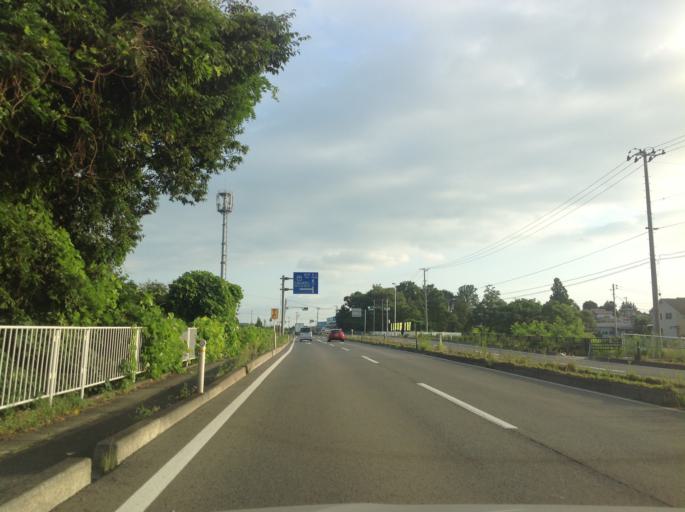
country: JP
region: Iwate
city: Hanamaki
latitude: 39.4940
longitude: 141.1430
